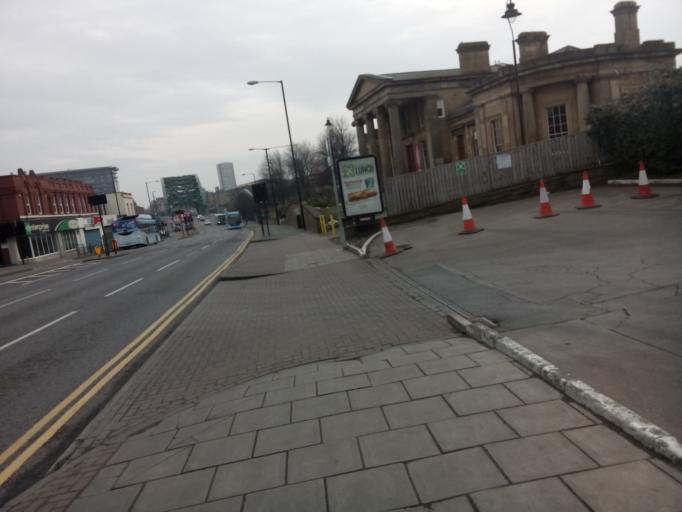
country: GB
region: England
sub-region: Sunderland
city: Sunderland
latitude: 54.9126
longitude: -1.3834
